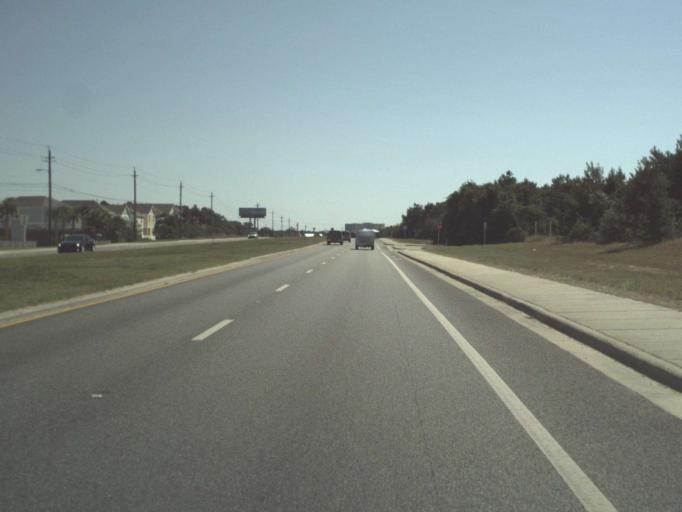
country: US
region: Florida
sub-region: Bay County
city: Laguna Beach
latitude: 30.2776
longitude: -86.0071
